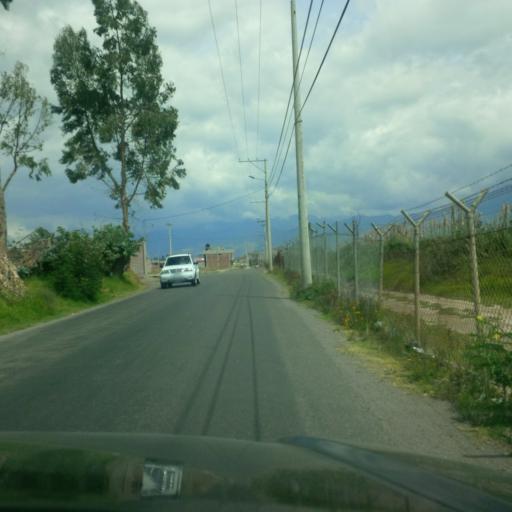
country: EC
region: Chimborazo
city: Riobamba
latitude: -1.6430
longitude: -78.6613
